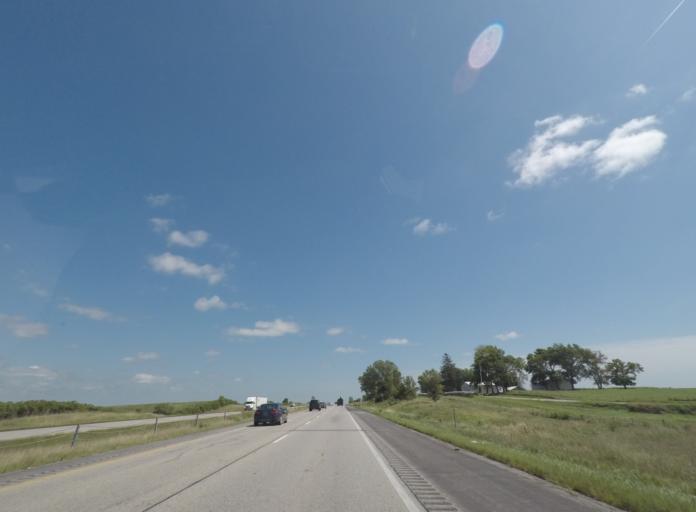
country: US
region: Iowa
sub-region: Iowa County
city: Williamsburg
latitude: 41.6869
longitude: -91.8425
